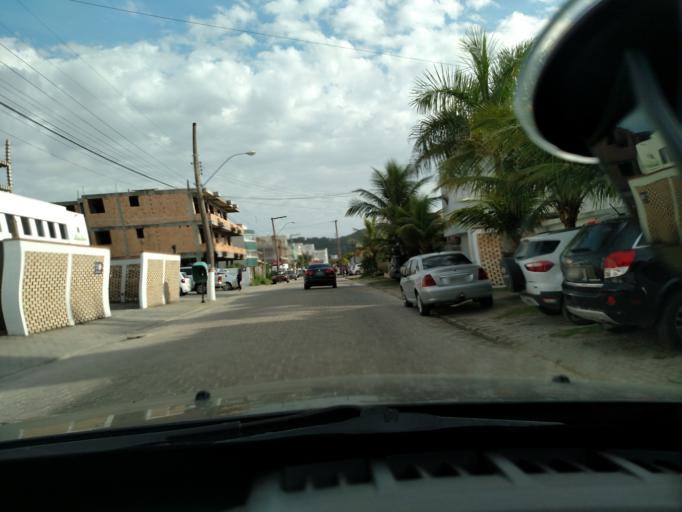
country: BR
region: Santa Catarina
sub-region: Porto Belo
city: Porto Belo
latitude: -27.1792
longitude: -48.5007
